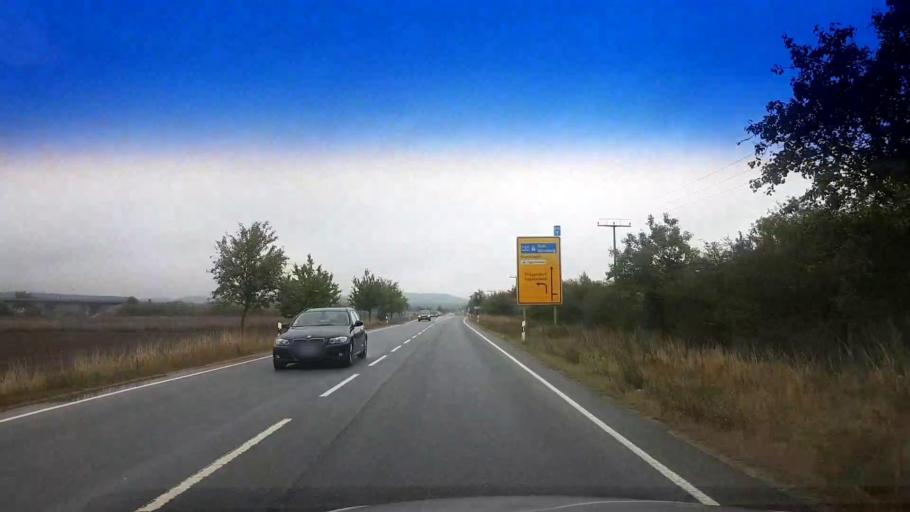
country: DE
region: Bavaria
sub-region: Upper Franconia
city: Eggolsheim
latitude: 49.7650
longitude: 11.0420
